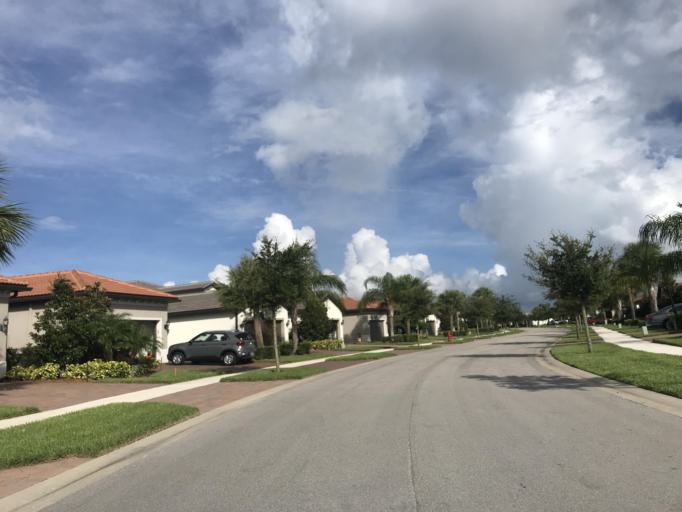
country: US
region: Florida
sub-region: Indian River County
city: Gifford
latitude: 27.6868
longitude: -80.4302
